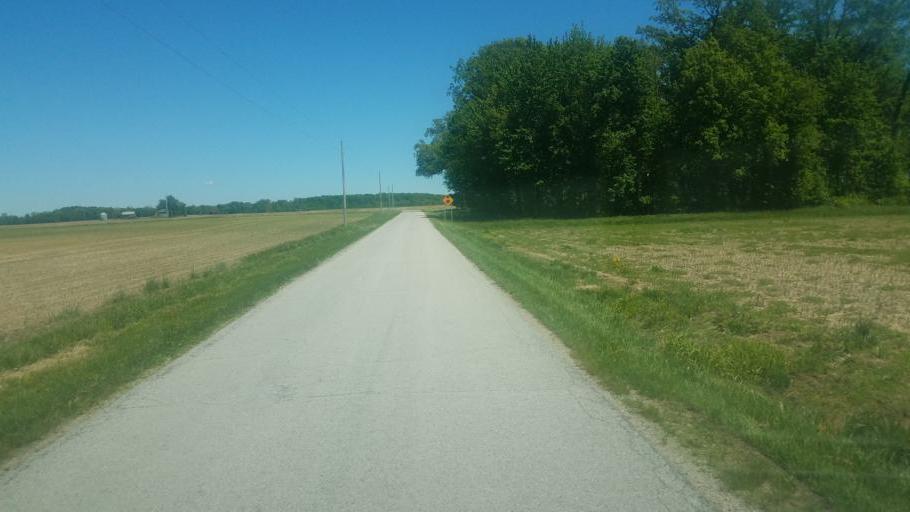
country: US
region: Ohio
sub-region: Champaign County
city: Saint Paris
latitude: 40.1986
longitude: -84.0243
